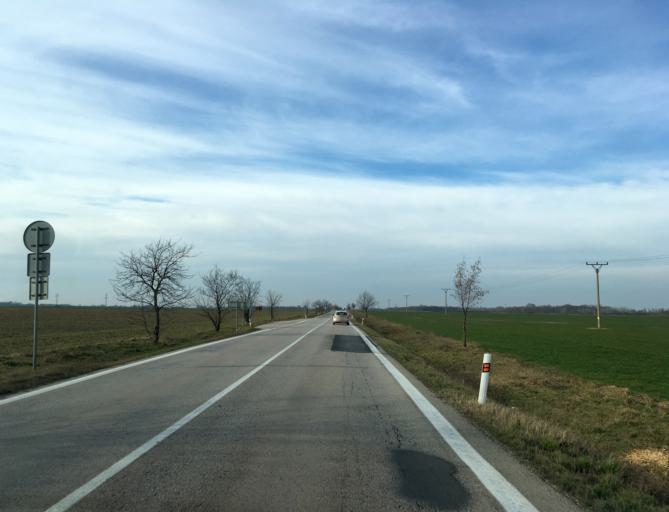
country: SK
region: Nitriansky
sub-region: Okres Nove Zamky
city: Nove Zamky
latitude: 48.0402
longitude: 18.1226
